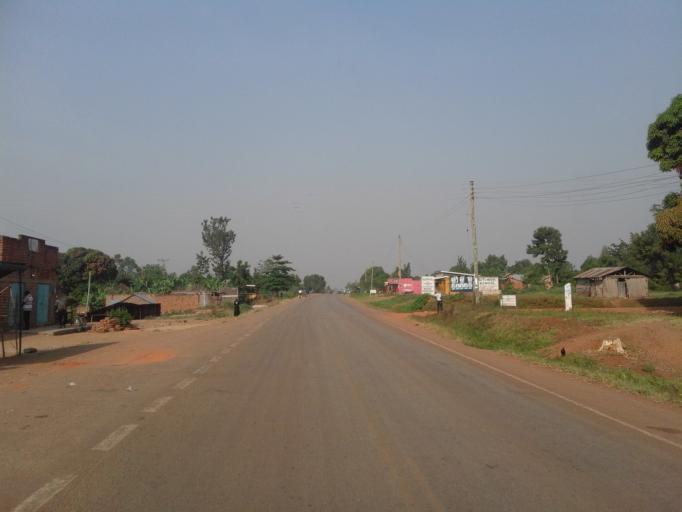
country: UG
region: Eastern Region
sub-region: Mbale District
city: Mbale
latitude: 1.0739
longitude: 34.1201
